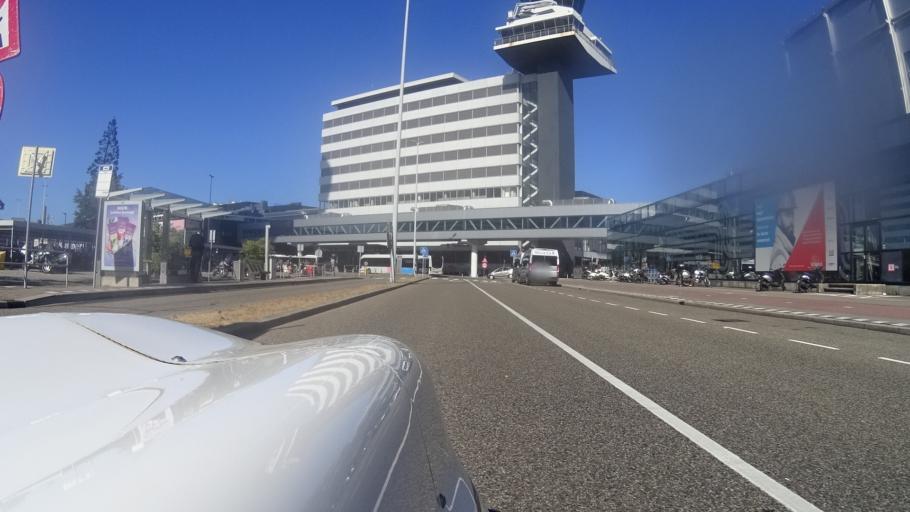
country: NL
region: North Holland
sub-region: Gemeente Aalsmeer
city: Aalsmeer
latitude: 52.3068
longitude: 4.7623
